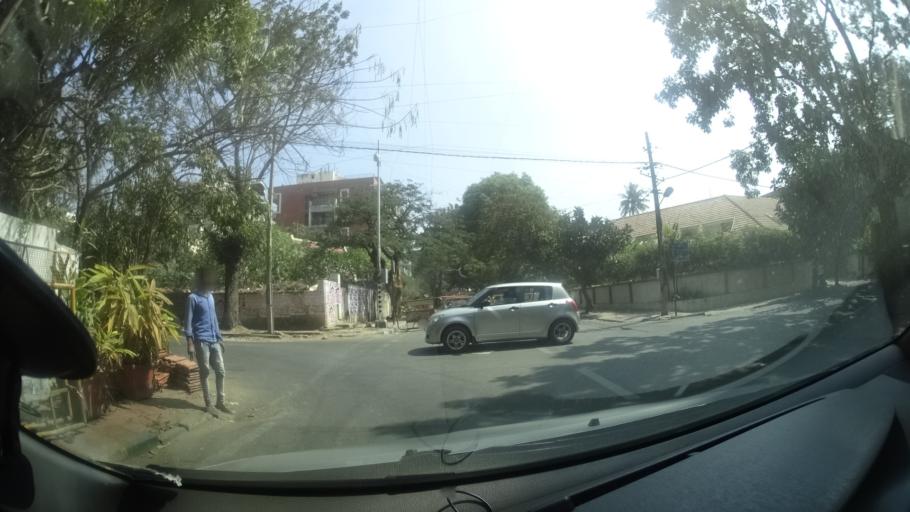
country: IN
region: Karnataka
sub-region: Bangalore Urban
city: Bangalore
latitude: 13.0091
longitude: 77.5826
